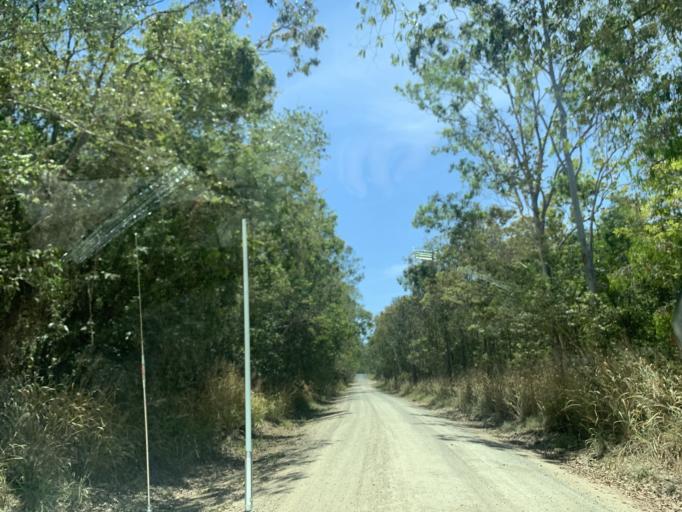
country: AU
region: Queensland
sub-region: Tablelands
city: Kuranda
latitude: -16.9221
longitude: 145.5869
